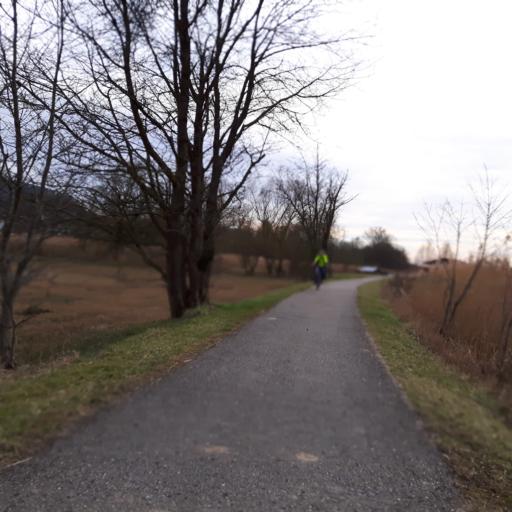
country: DE
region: Baden-Wuerttemberg
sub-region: Regierungsbezirk Stuttgart
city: Oberstenfeld
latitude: 49.0138
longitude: 9.3131
